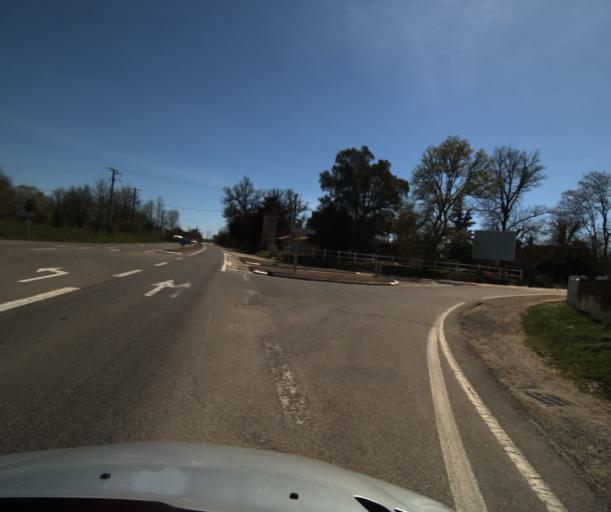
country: FR
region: Midi-Pyrenees
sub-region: Departement du Tarn-et-Garonne
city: Montbeton
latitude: 44.0325
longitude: 1.3153
